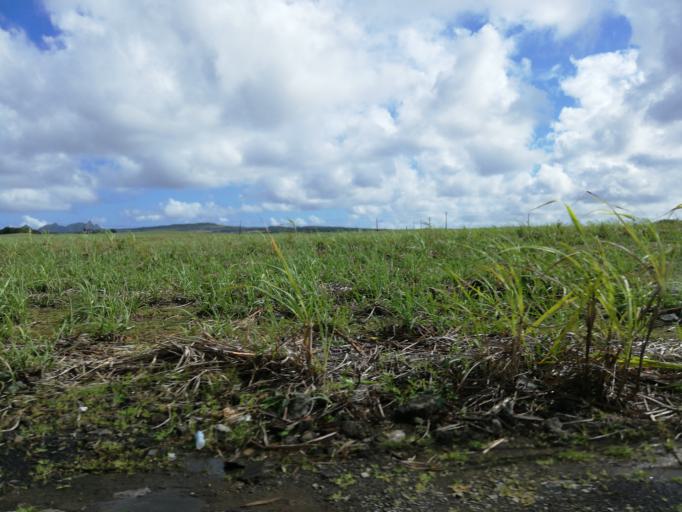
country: MU
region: Moka
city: Providence
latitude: -20.2471
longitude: 57.6192
